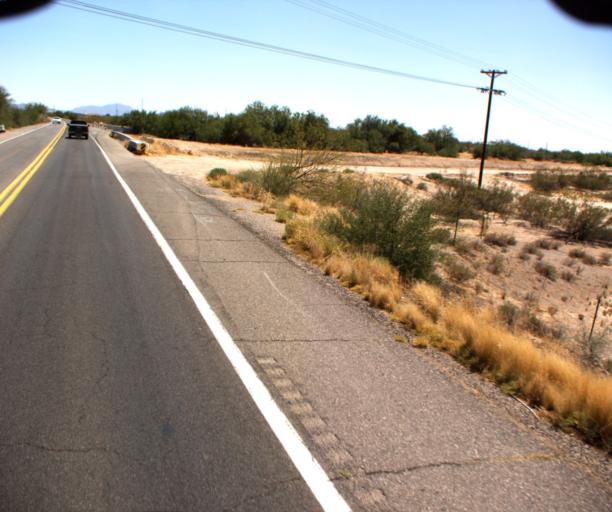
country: US
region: Arizona
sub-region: Pinal County
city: Florence
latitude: 33.0190
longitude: -111.3792
